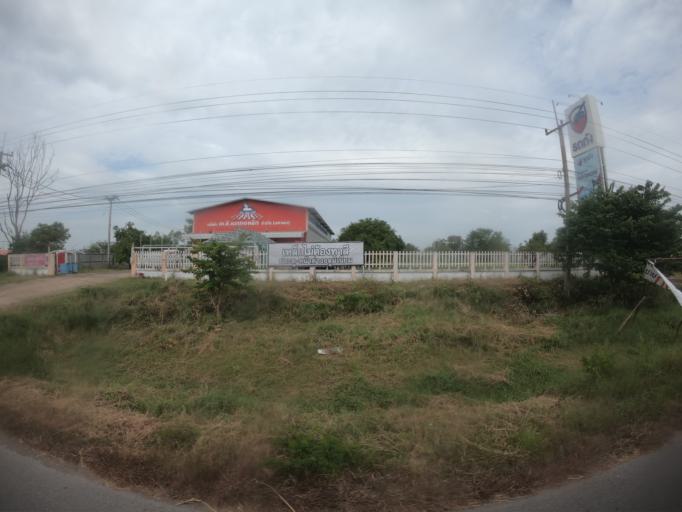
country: TH
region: Roi Et
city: Changhan
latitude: 16.0875
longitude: 103.5578
